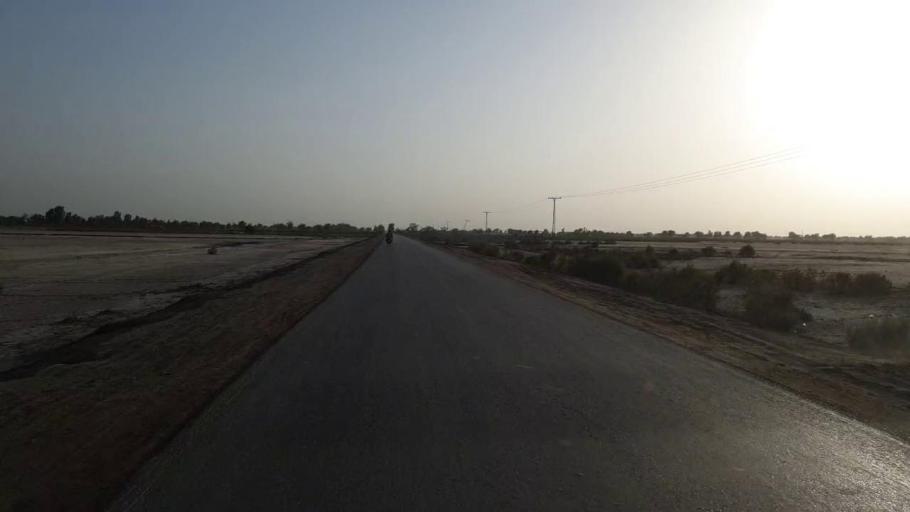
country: PK
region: Sindh
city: Jam Sahib
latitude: 26.2891
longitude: 68.6051
